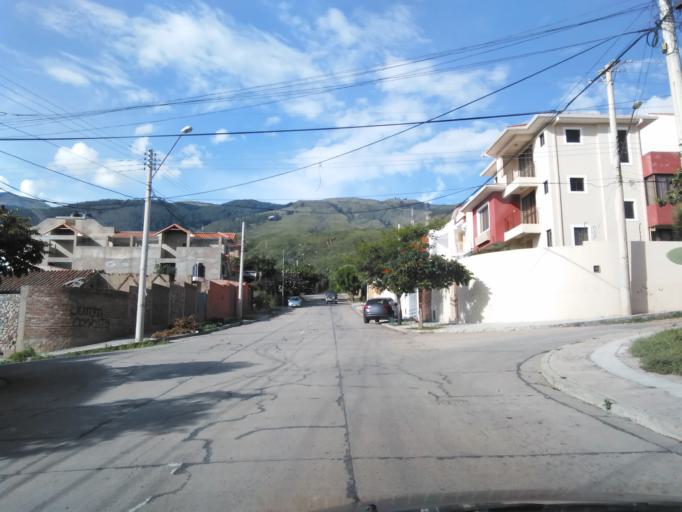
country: BO
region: Cochabamba
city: Cochabamba
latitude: -17.3653
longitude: -66.1449
